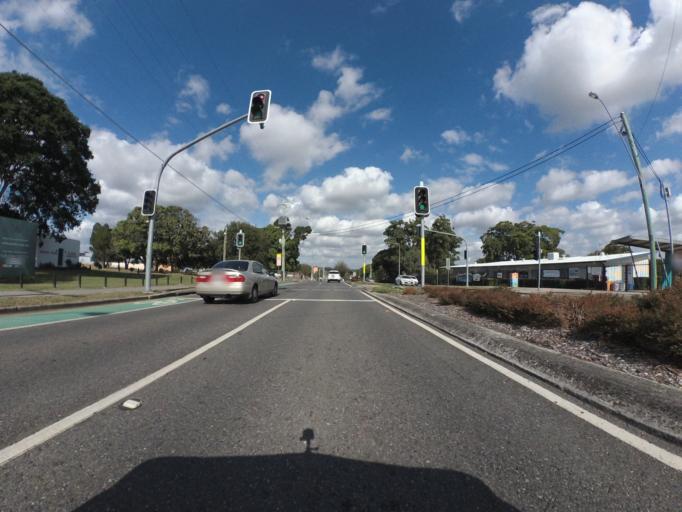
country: AU
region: Queensland
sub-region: Brisbane
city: Wynnum West
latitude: -27.4546
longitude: 153.1550
